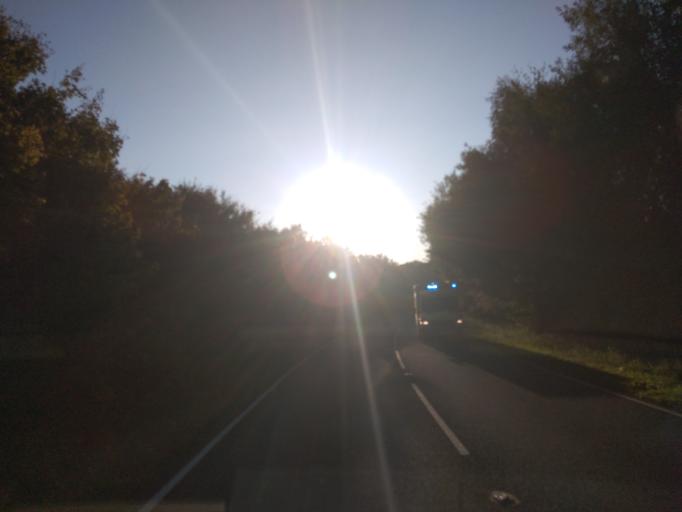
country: GB
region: England
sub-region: West Sussex
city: Goring-by-Sea
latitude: 50.8388
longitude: -0.4460
